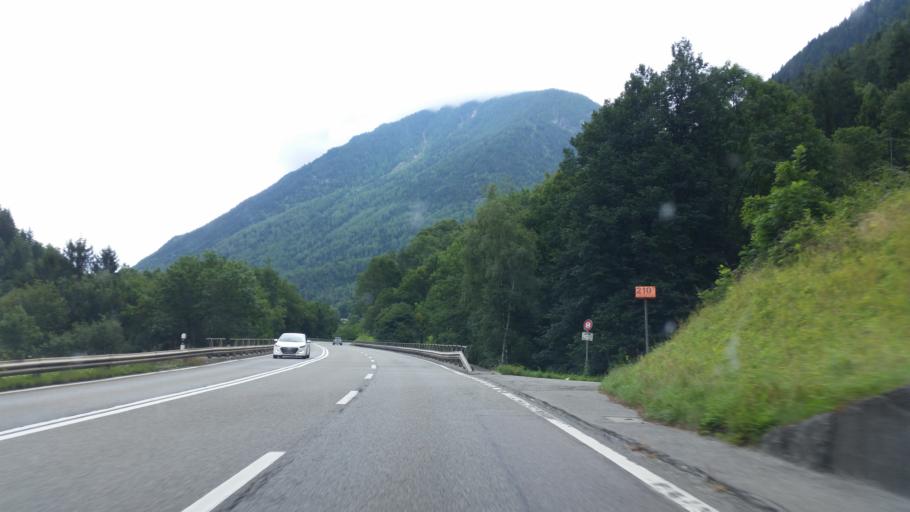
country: CH
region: Valais
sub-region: Martigny District
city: Martigny-Combe
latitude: 46.0735
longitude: 7.0541
